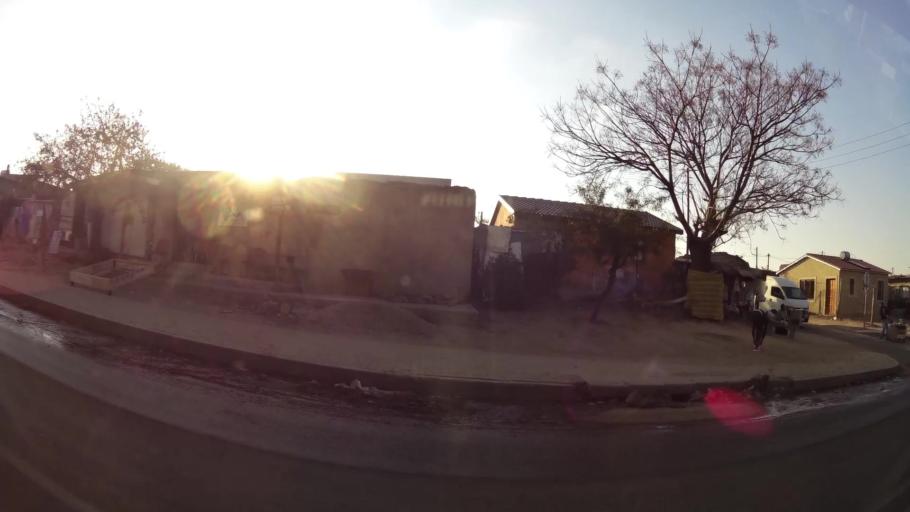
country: ZA
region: Gauteng
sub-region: Ekurhuleni Metropolitan Municipality
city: Tembisa
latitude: -26.0184
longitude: 28.1794
